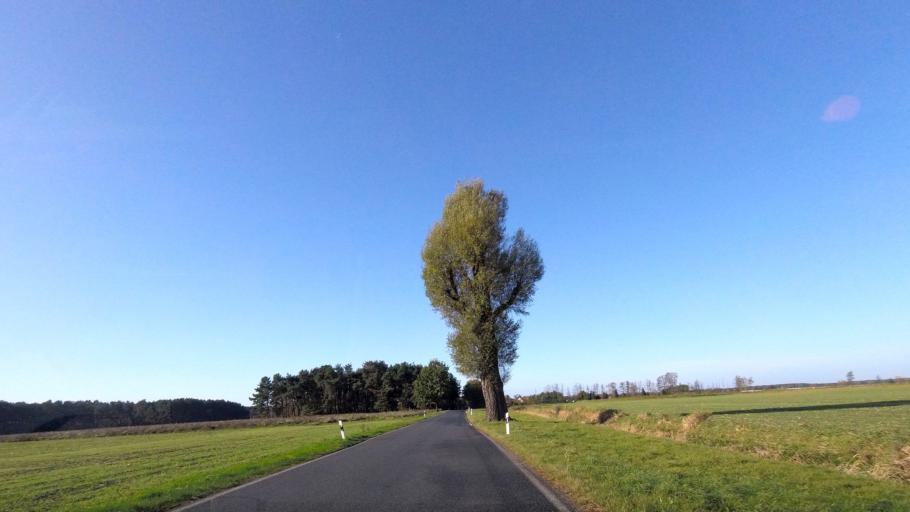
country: DE
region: Brandenburg
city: Beelitz
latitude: 52.1865
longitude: 12.9371
